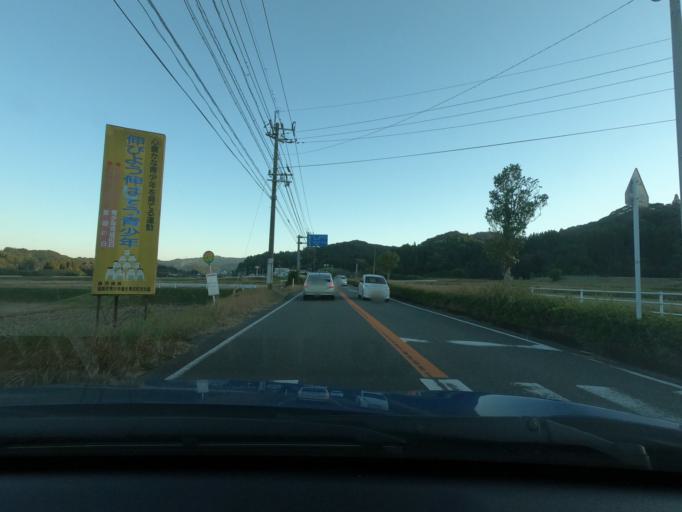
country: JP
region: Kagoshima
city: Satsumasendai
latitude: 31.8013
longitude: 130.3992
